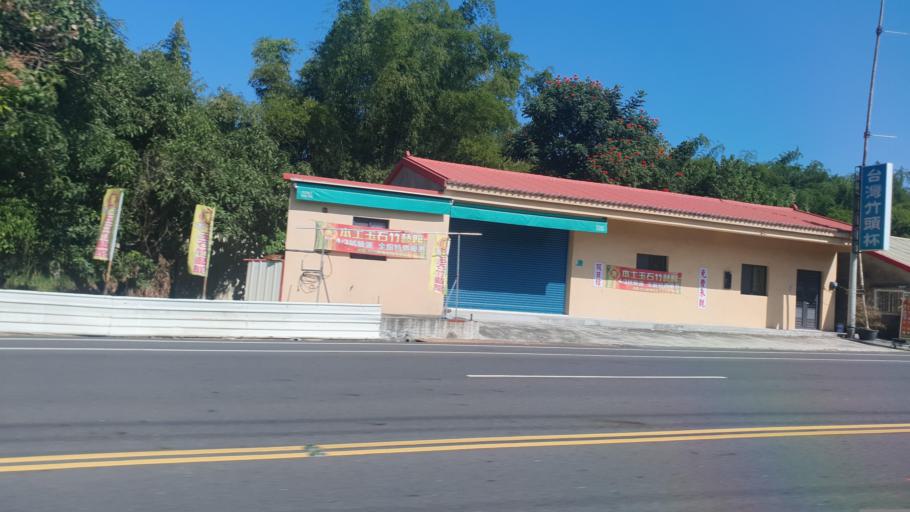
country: TW
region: Taiwan
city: Yujing
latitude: 23.0608
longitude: 120.3911
